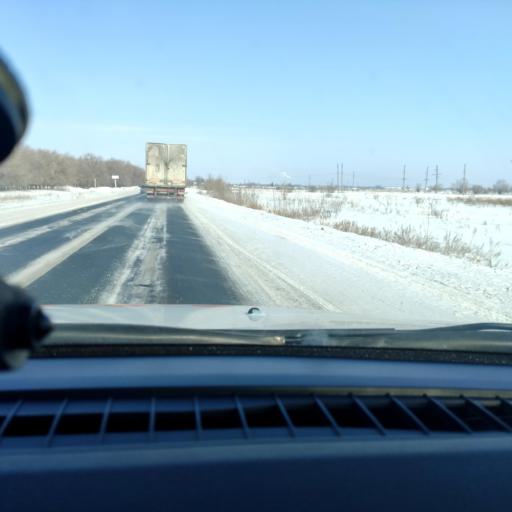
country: RU
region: Samara
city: Smyshlyayevka
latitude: 53.1726
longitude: 50.4574
